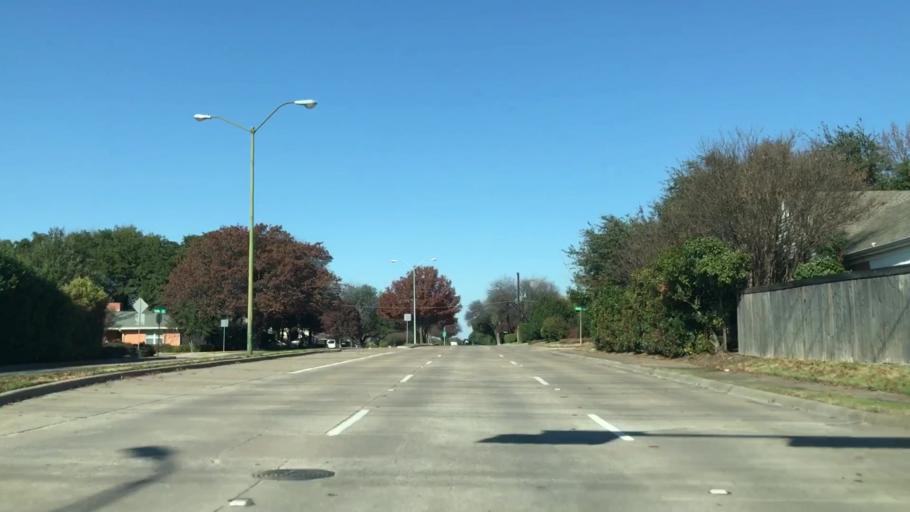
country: US
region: Texas
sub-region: Dallas County
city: University Park
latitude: 32.8968
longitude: -96.7879
